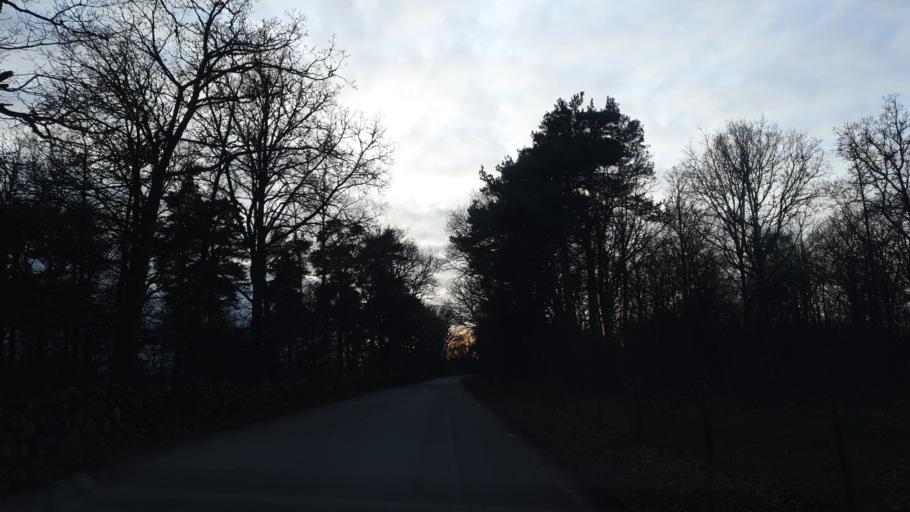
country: SE
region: Blekinge
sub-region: Karlskrona Kommun
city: Jaemjoe
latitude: 56.1604
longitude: 15.9150
